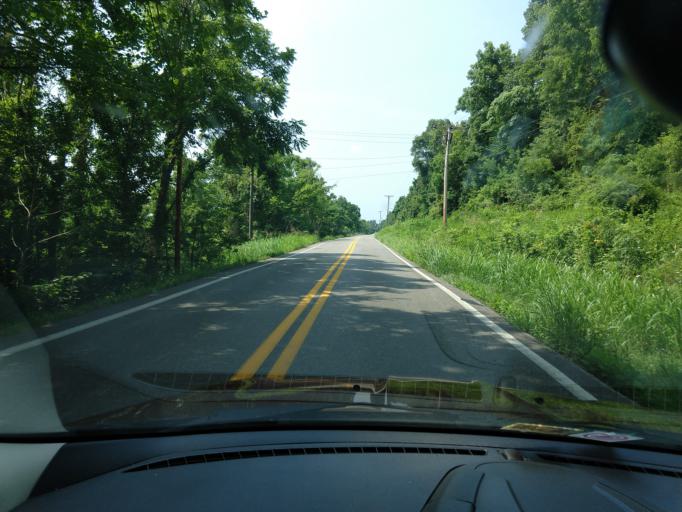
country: US
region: West Virginia
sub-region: Mason County
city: New Haven
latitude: 38.9202
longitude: -81.9148
